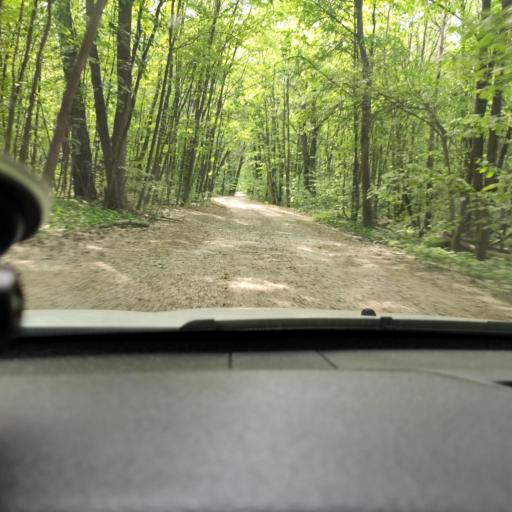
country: RU
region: Samara
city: Novosemeykino
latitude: 53.3273
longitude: 50.2187
